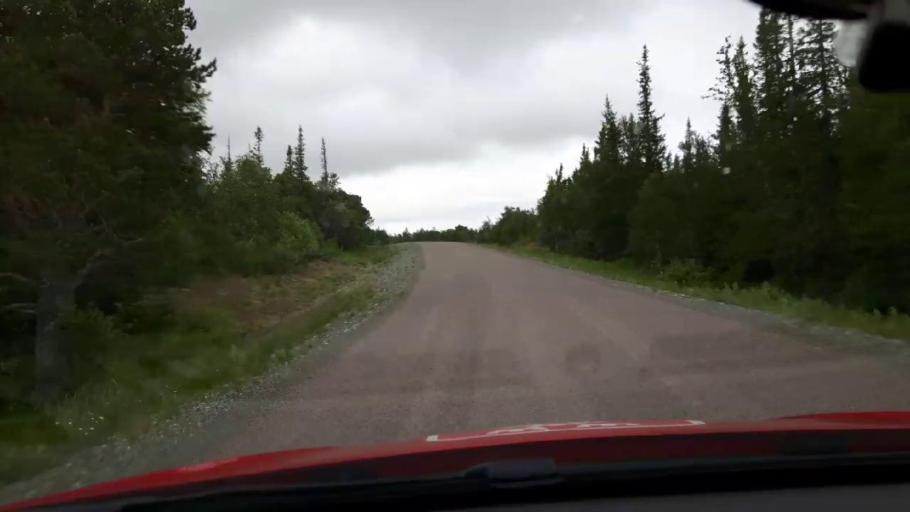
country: SE
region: Jaemtland
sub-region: Are Kommun
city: Are
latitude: 63.2501
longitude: 12.4267
